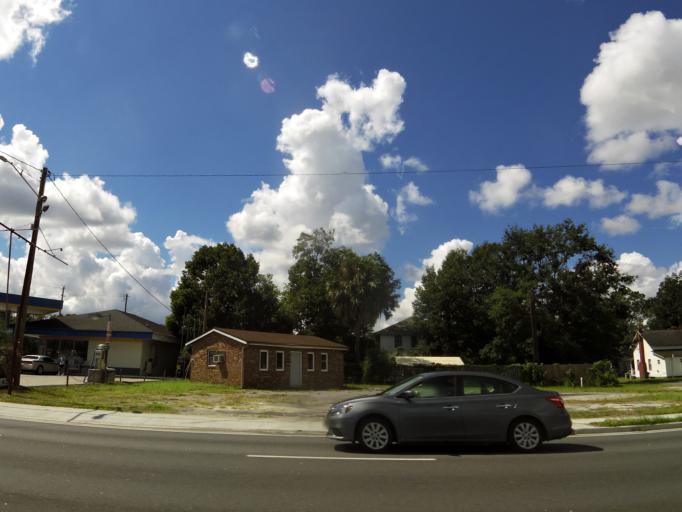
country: US
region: Georgia
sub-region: Charlton County
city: Folkston
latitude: 30.8300
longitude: -82.0057
